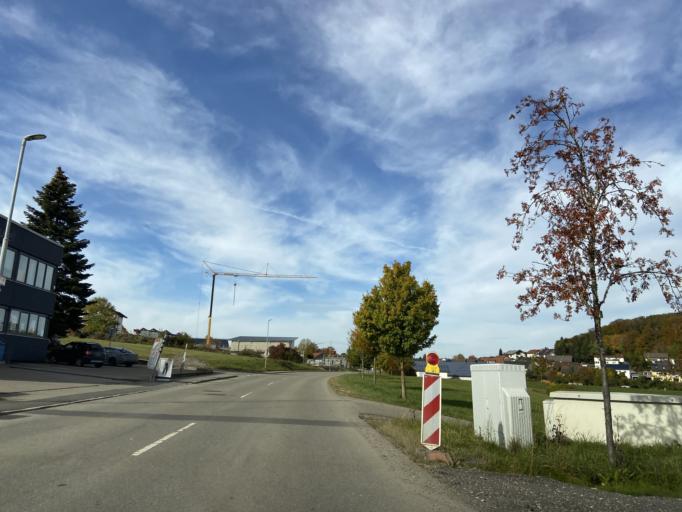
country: DE
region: Baden-Wuerttemberg
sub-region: Tuebingen Region
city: Schwenningen
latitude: 48.1058
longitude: 9.0063
